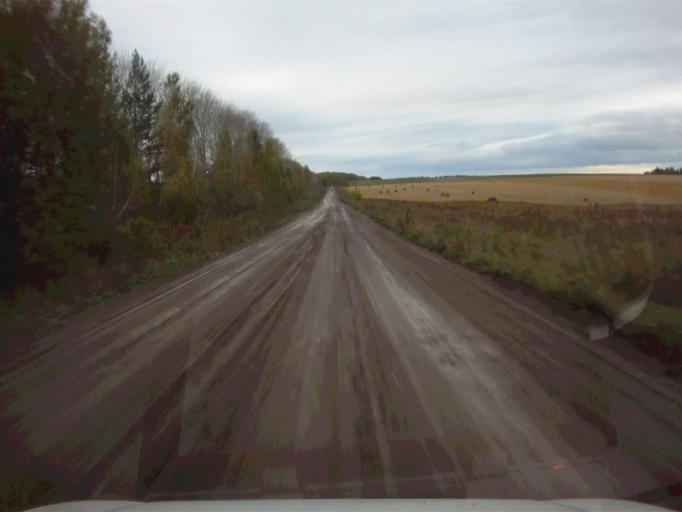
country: RU
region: Sverdlovsk
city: Mikhaylovsk
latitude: 56.1629
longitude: 59.2424
